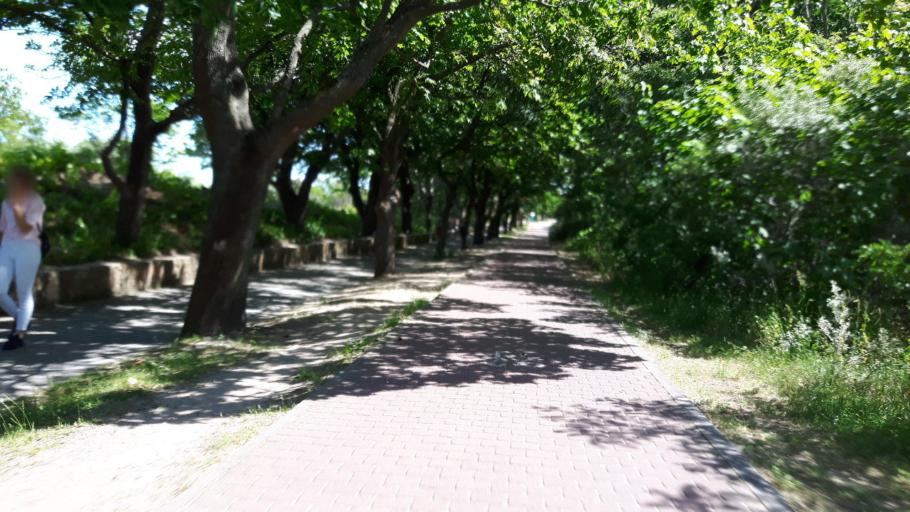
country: PL
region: Pomeranian Voivodeship
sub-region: Sopot
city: Sopot
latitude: 54.4304
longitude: 18.5897
